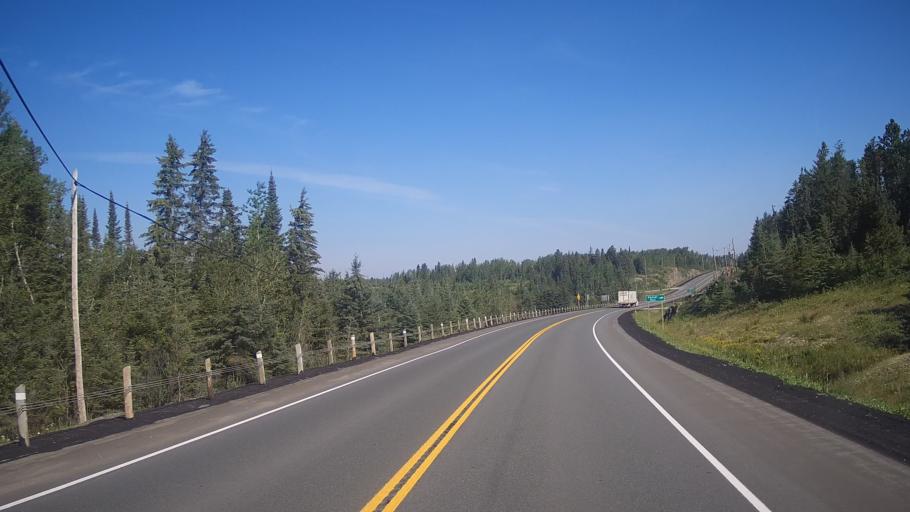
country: CA
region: Ontario
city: Dryden
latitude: 49.6514
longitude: -92.4738
